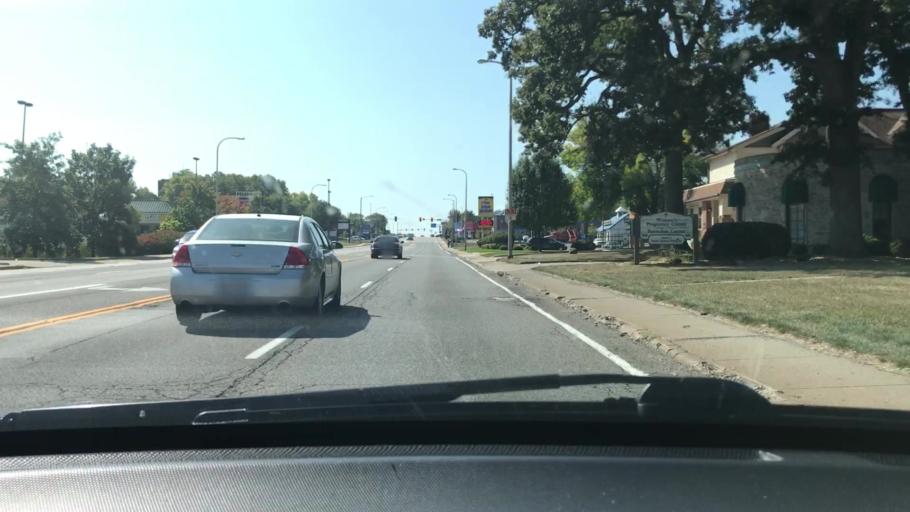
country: US
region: Illinois
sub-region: Peoria County
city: North Peoria
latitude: 40.7101
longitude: -89.5941
